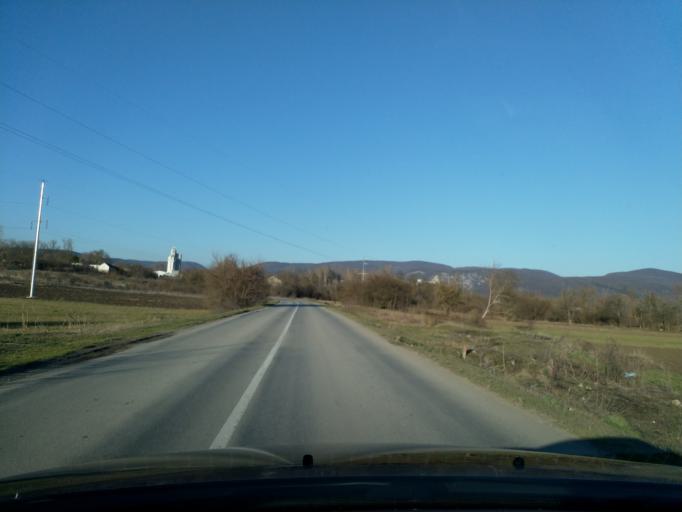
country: RS
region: Central Serbia
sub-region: Pomoravski Okrug
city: Paracin
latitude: 43.8997
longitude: 21.4934
